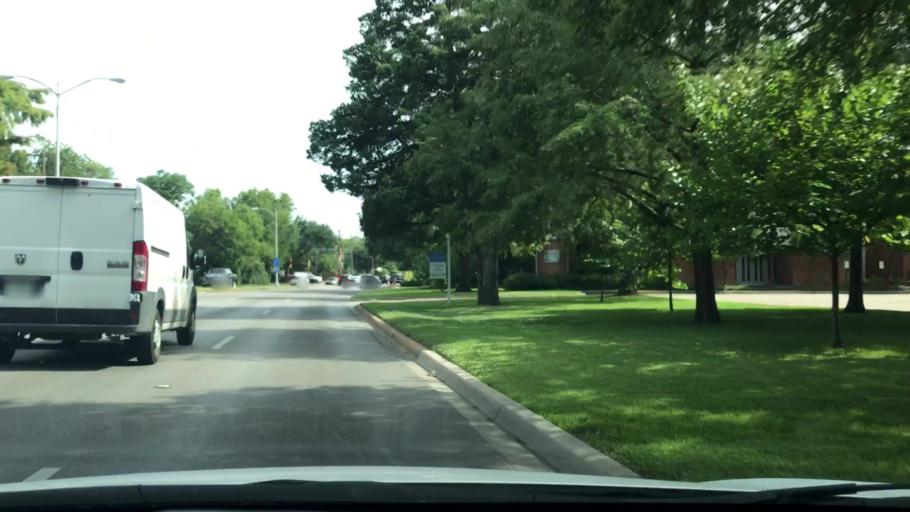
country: US
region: Texas
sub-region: Dallas County
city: University Park
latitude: 32.8383
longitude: -96.8218
